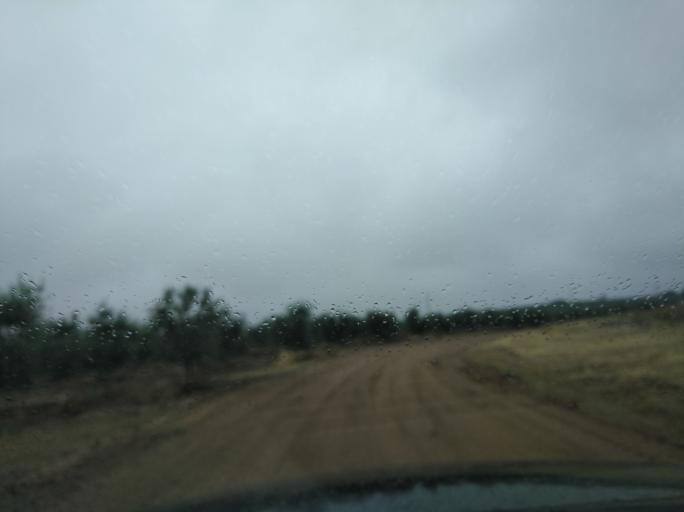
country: PT
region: Portalegre
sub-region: Campo Maior
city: Campo Maior
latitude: 38.9530
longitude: -7.0565
